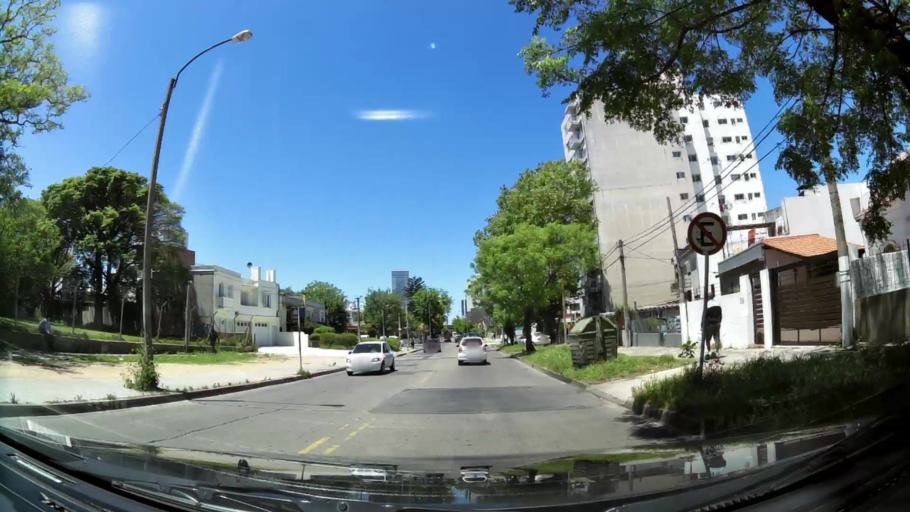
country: UY
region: Montevideo
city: Montevideo
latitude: -34.8986
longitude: -56.1406
